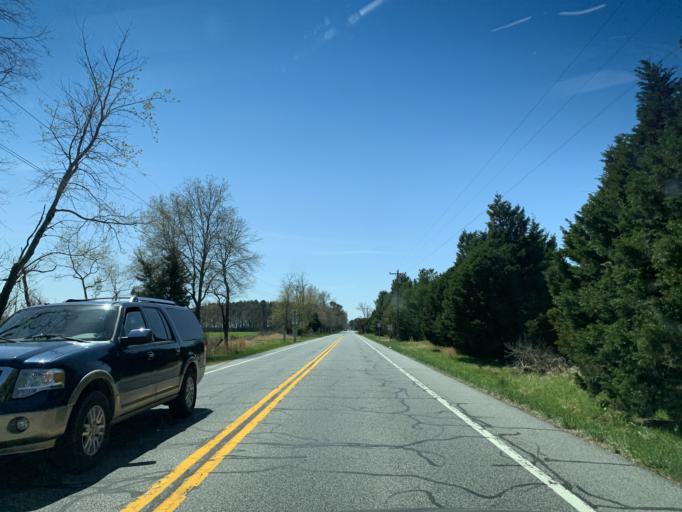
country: US
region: Maryland
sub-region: Talbot County
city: Easton
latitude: 38.8610
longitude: -76.0080
